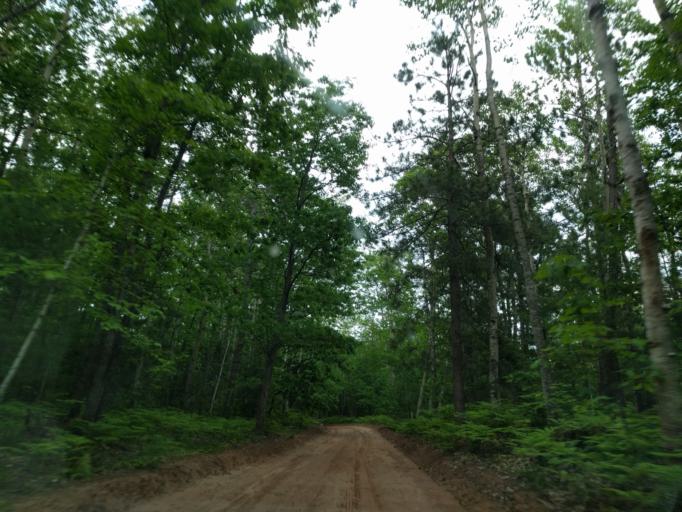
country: US
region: Michigan
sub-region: Marquette County
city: Trowbridge Park
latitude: 46.6170
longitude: -87.5068
